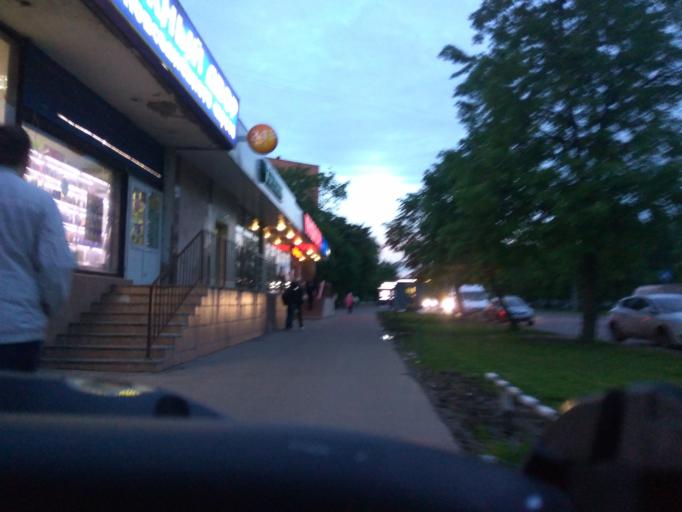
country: RU
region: Moscow
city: Kolomenskoye
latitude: 55.6686
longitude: 37.6485
